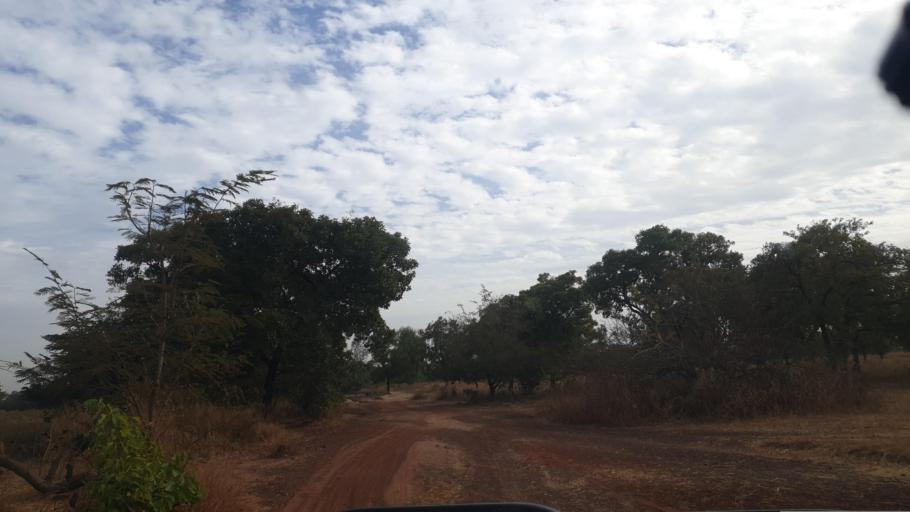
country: ML
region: Sikasso
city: Yanfolila
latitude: 11.4068
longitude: -8.0111
